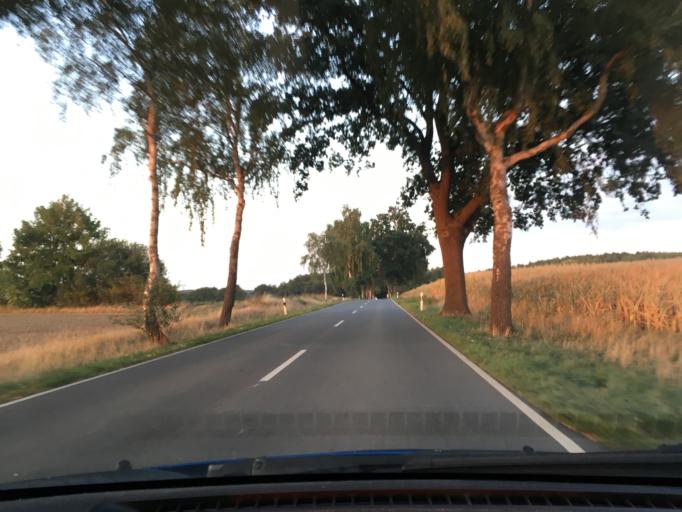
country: DE
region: Lower Saxony
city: Hitzacker
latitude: 53.1415
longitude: 10.9821
